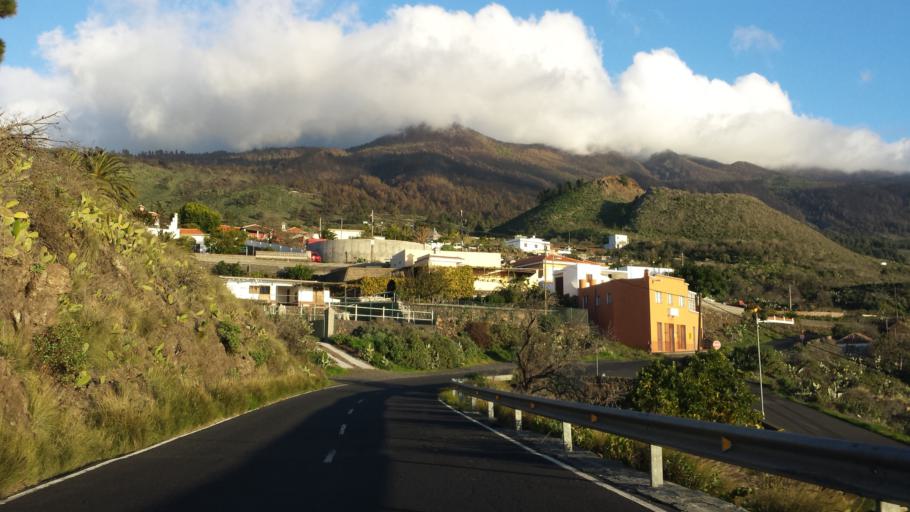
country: ES
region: Canary Islands
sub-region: Provincia de Santa Cruz de Tenerife
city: El Paso
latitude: 28.6162
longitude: -17.8843
